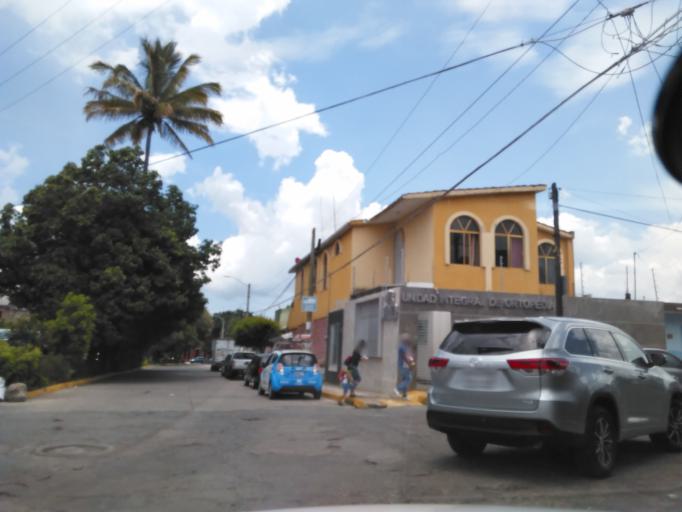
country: MX
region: Nayarit
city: Tepic
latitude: 21.4967
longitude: -104.8890
